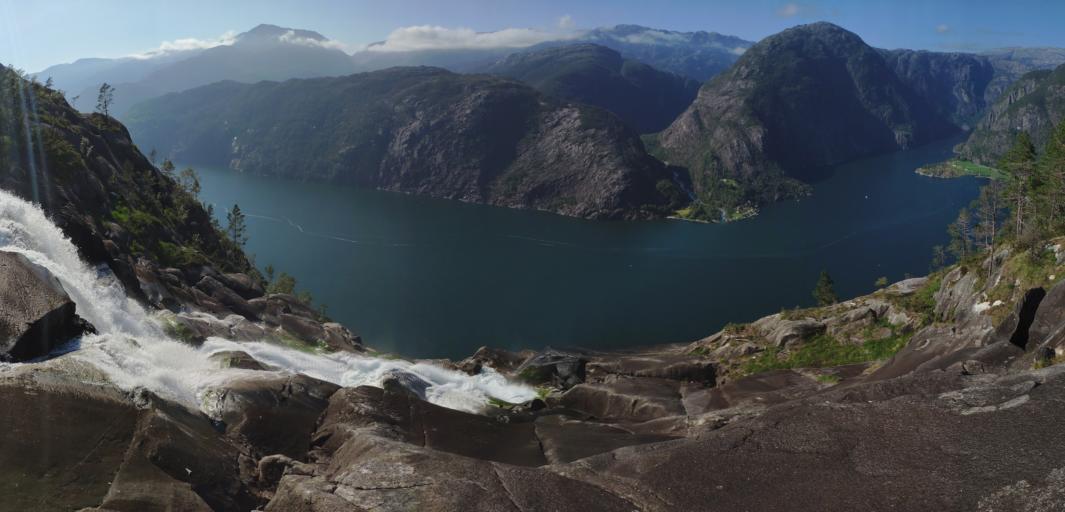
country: NO
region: Rogaland
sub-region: Sauda
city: Sauda
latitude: 59.8427
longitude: 6.3417
